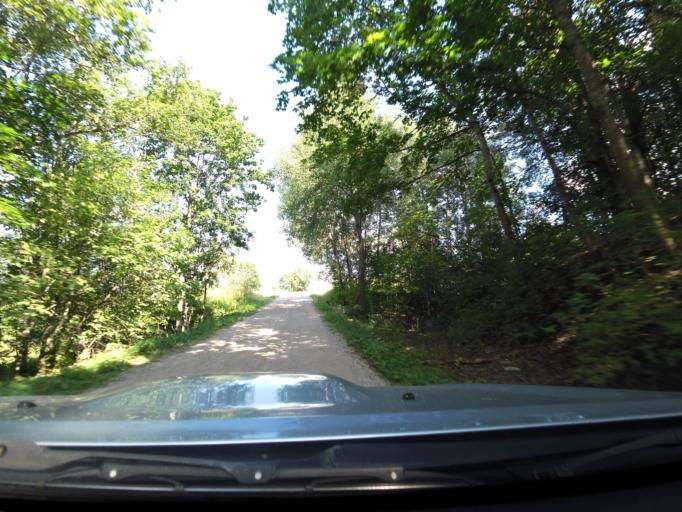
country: LT
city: Grigiskes
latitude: 54.8184
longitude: 24.9705
